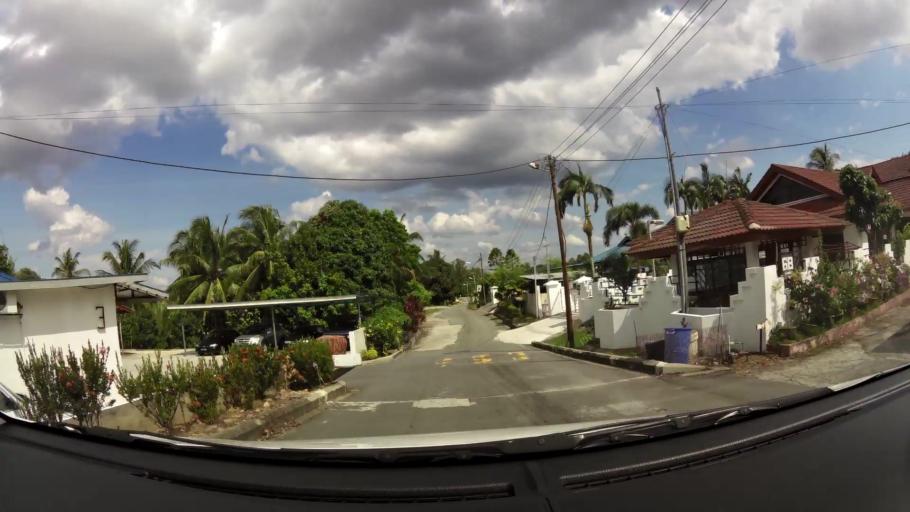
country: BN
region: Brunei and Muara
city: Bandar Seri Begawan
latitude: 4.9563
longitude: 114.9553
